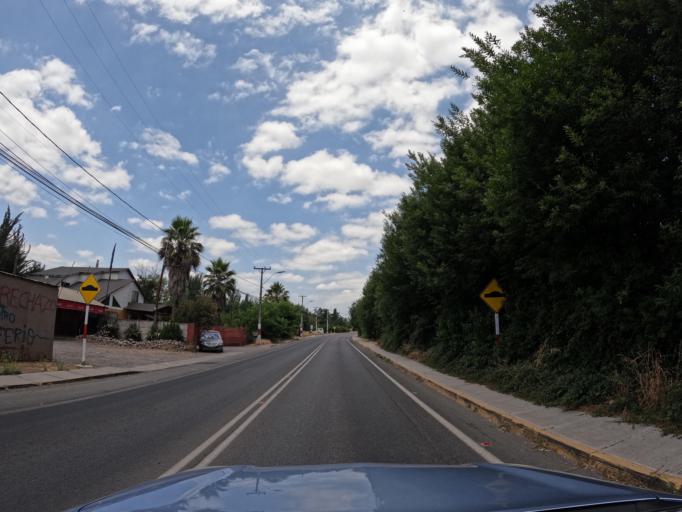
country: CL
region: Maule
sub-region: Provincia de Curico
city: Curico
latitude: -35.0005
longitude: -71.2330
